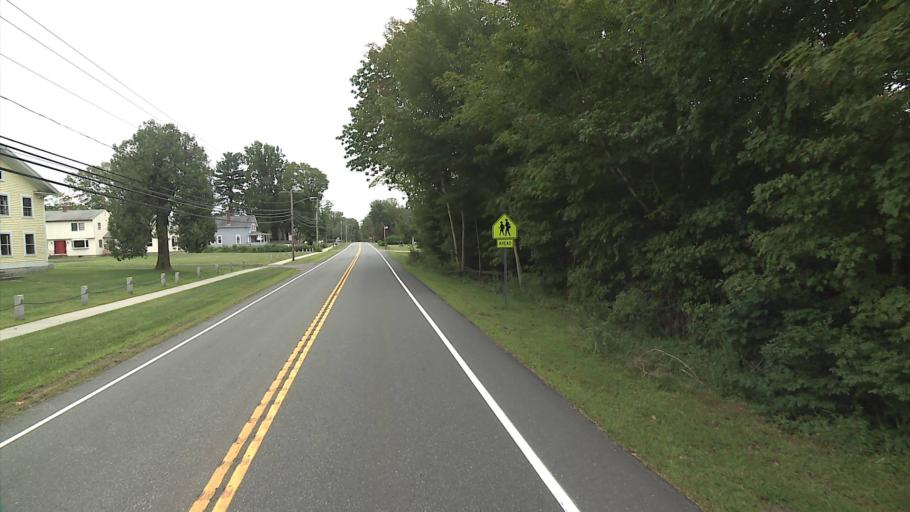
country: US
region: Connecticut
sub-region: New London County
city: Colchester
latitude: 41.4902
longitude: -72.2759
